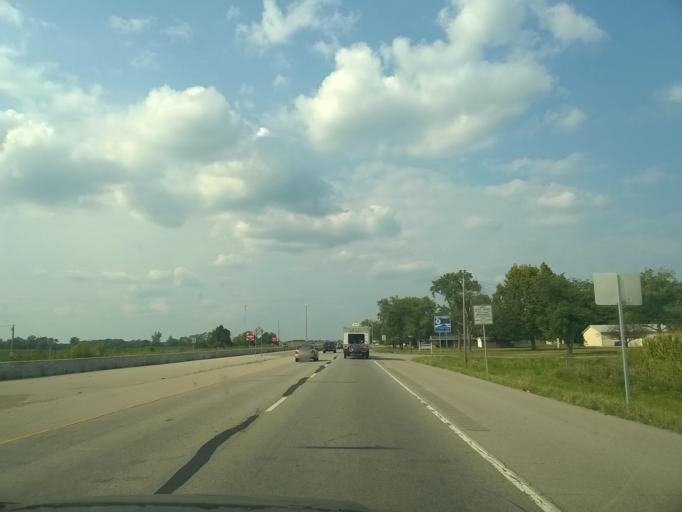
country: US
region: Indiana
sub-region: Vigo County
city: Terre Haute
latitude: 39.3635
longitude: -87.3882
